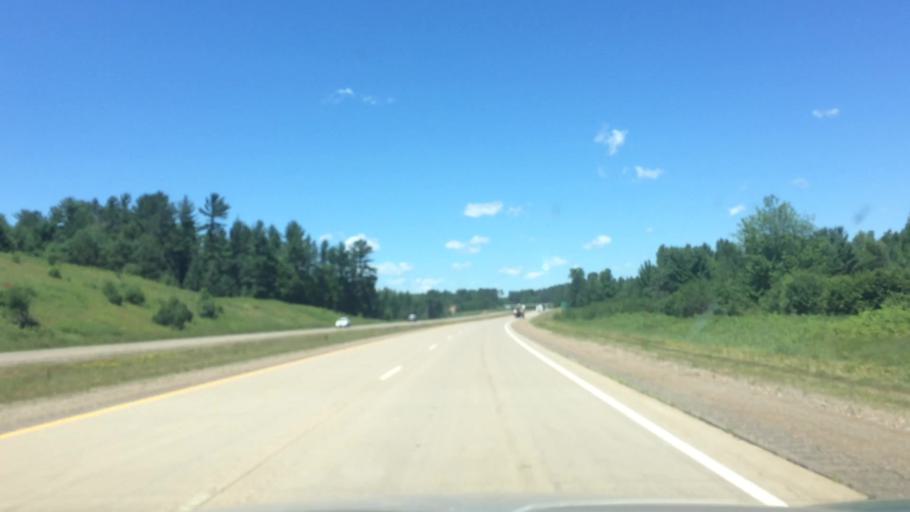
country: US
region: Wisconsin
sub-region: Lincoln County
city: Tomahawk
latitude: 45.4285
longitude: -89.6777
